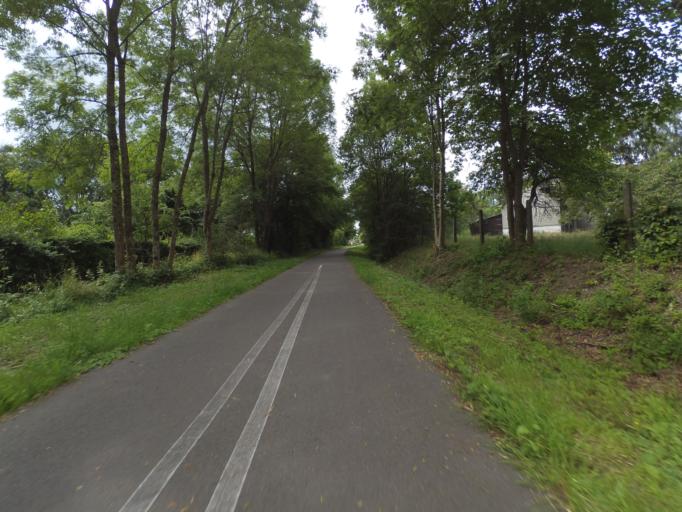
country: DE
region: North Rhine-Westphalia
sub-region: Regierungsbezirk Koln
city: Roetgen
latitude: 50.6397
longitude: 6.1906
